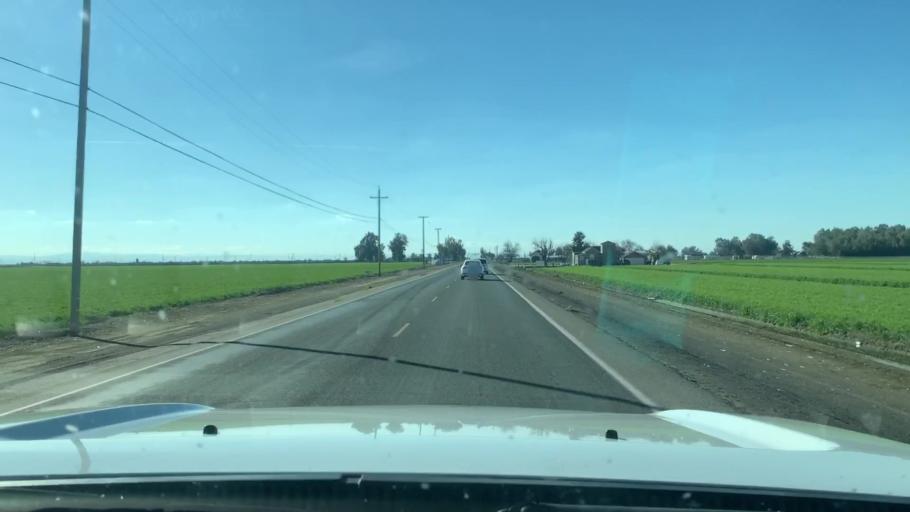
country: US
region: California
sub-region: Kings County
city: Home Garden
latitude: 36.2112
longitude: -119.6296
